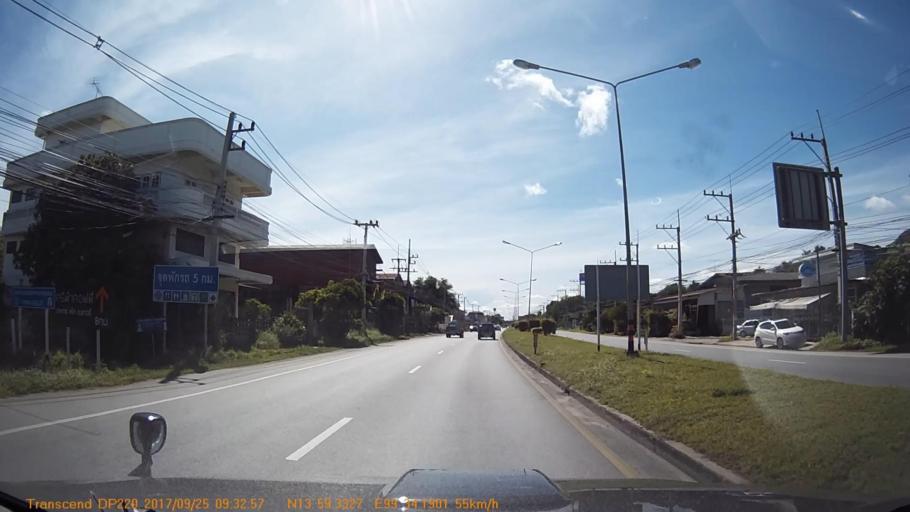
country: TH
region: Kanchanaburi
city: Kanchanaburi
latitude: 13.9888
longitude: 99.5700
